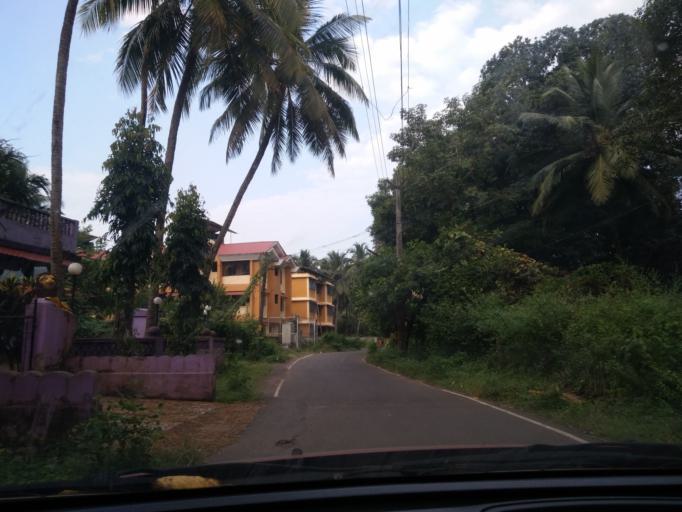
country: IN
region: Goa
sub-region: South Goa
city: Varca
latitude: 15.2313
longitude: 73.9471
